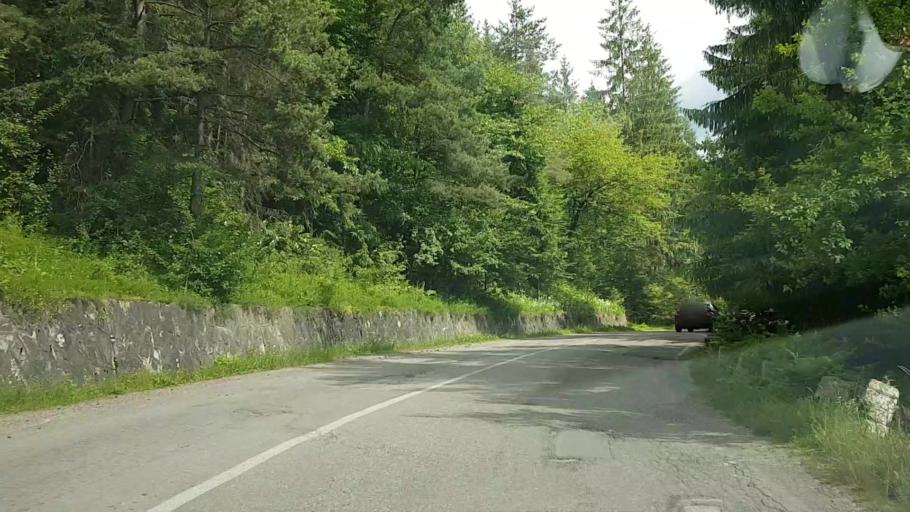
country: RO
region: Neamt
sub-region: Comuna Hangu
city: Hangu
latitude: 47.0056
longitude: 26.0974
